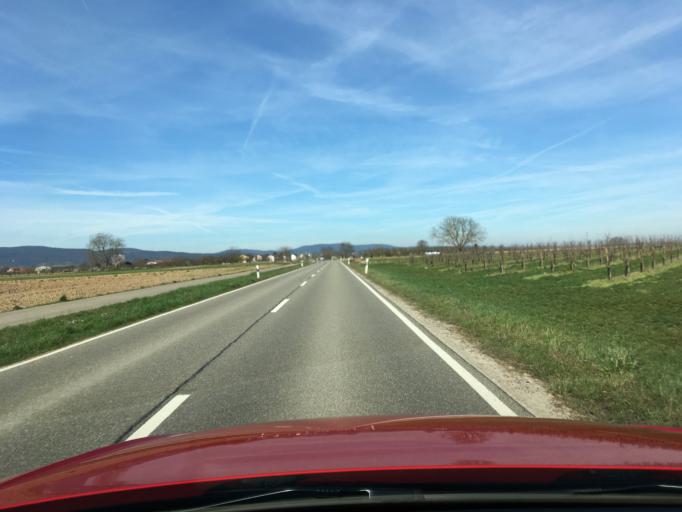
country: DE
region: Rheinland-Pfalz
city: Meckenheim
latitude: 49.4000
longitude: 8.2547
